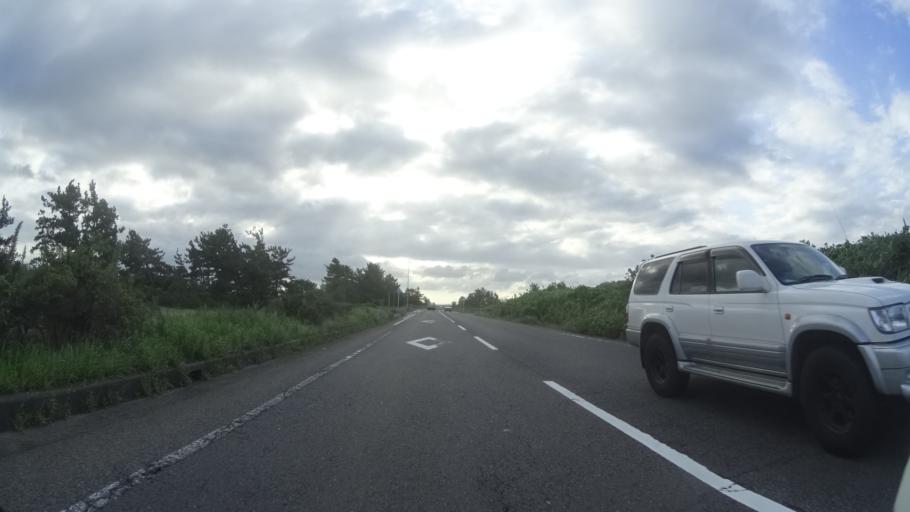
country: JP
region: Tottori
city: Kurayoshi
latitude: 35.4983
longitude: 133.7852
